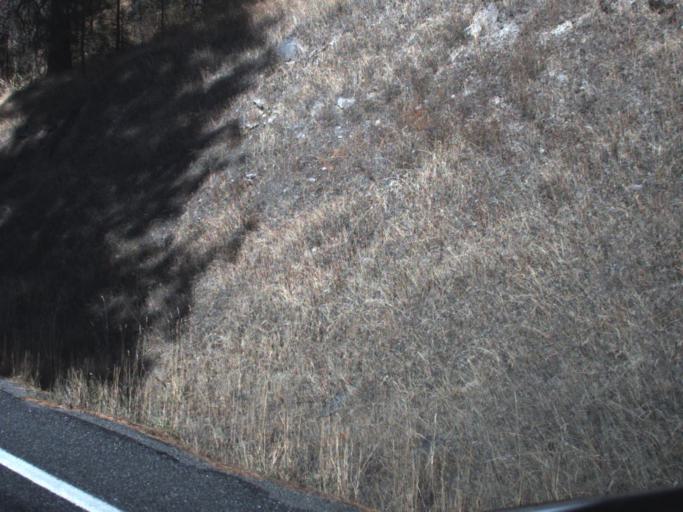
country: US
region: Washington
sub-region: Stevens County
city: Kettle Falls
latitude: 48.6463
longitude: -118.0805
